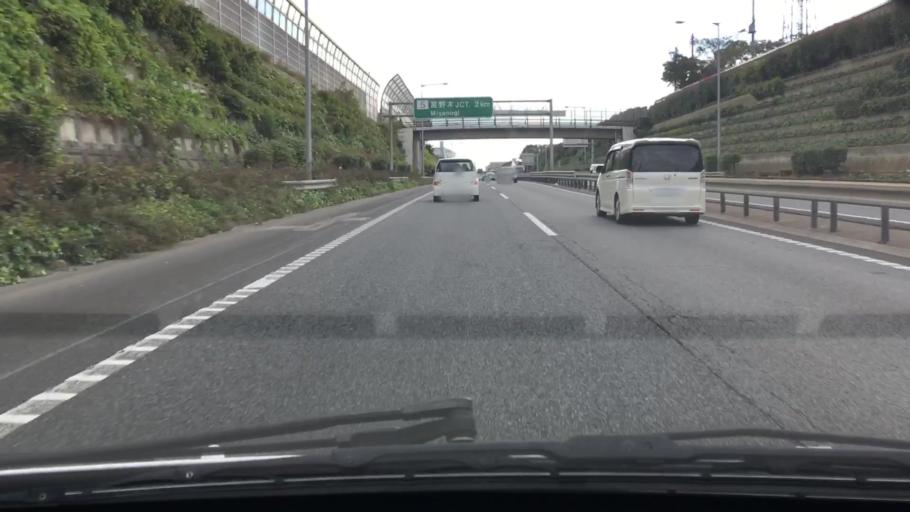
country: JP
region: Chiba
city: Chiba
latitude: 35.6675
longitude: 140.0726
